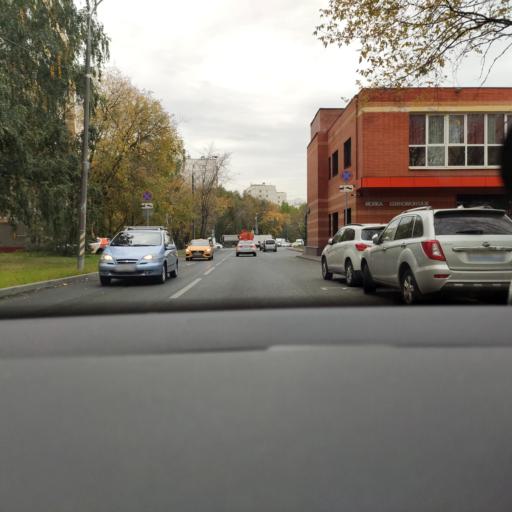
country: RU
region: Moscow
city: Kozeyevo
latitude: 55.8893
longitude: 37.6460
